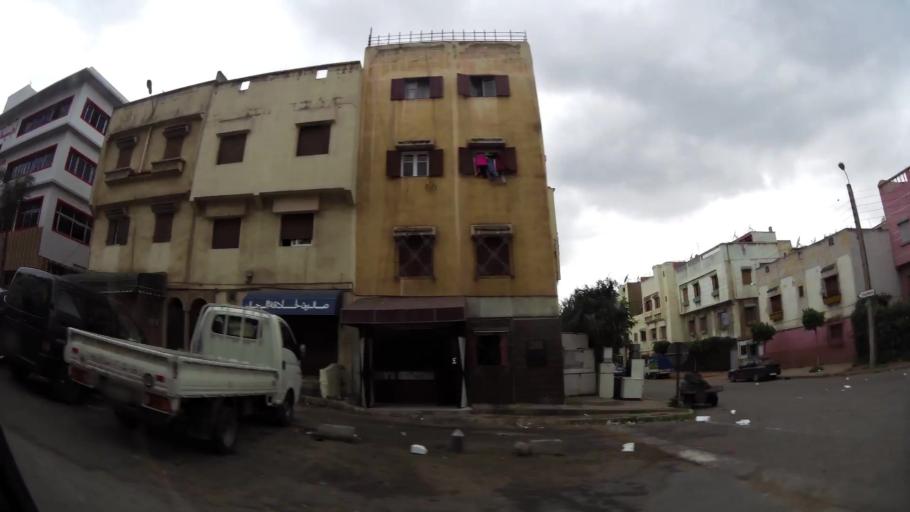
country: MA
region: Grand Casablanca
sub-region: Mediouna
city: Tit Mellil
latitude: 33.5708
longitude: -7.5398
